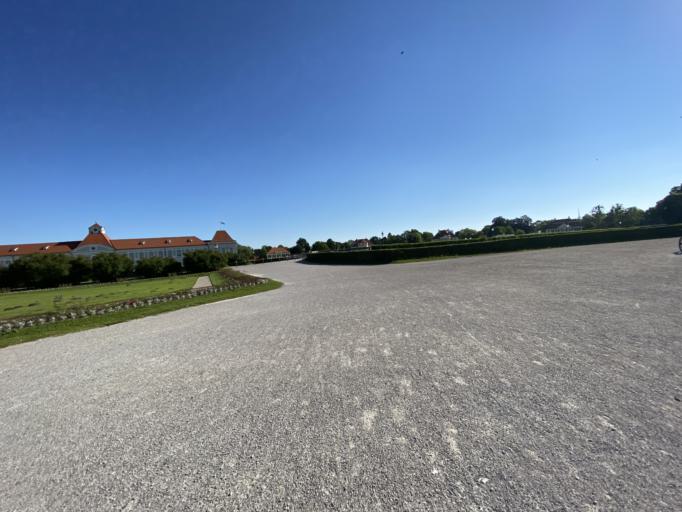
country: DE
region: Bavaria
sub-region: Upper Bavaria
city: Pasing
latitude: 48.1585
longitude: 11.5052
